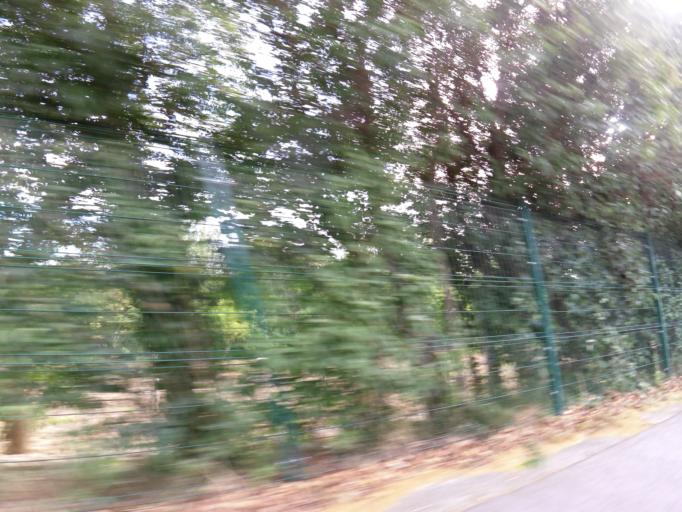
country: FR
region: Languedoc-Roussillon
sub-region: Departement du Gard
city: Saint-Mamert-du-Gard
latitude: 43.9099
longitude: 4.1998
